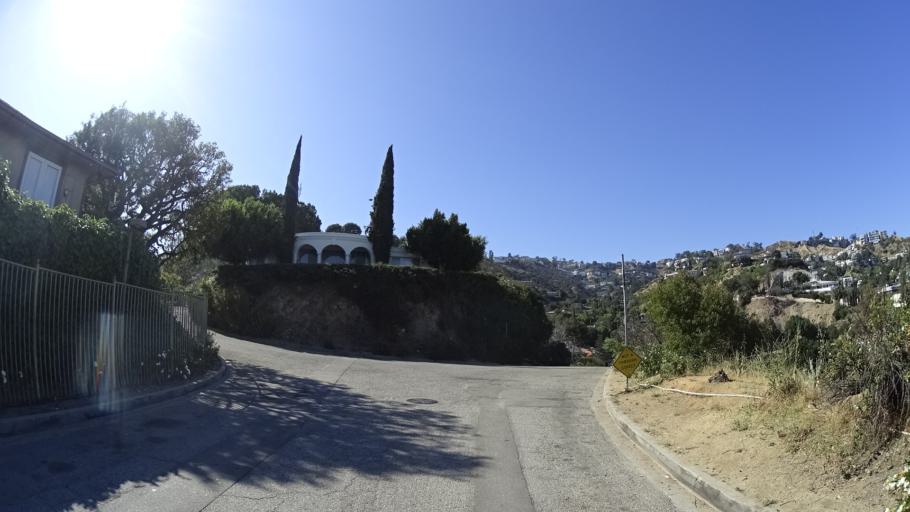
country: US
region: California
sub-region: Los Angeles County
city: West Hollywood
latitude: 34.0952
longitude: -118.3838
